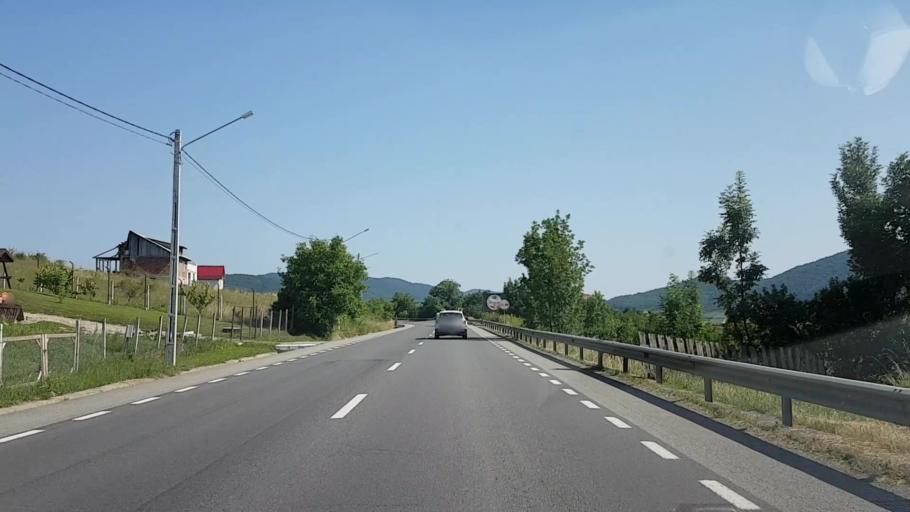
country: RO
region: Bistrita-Nasaud
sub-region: Comuna Sieu-Magherus
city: Sieu-Magherus
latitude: 47.0753
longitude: 24.3986
